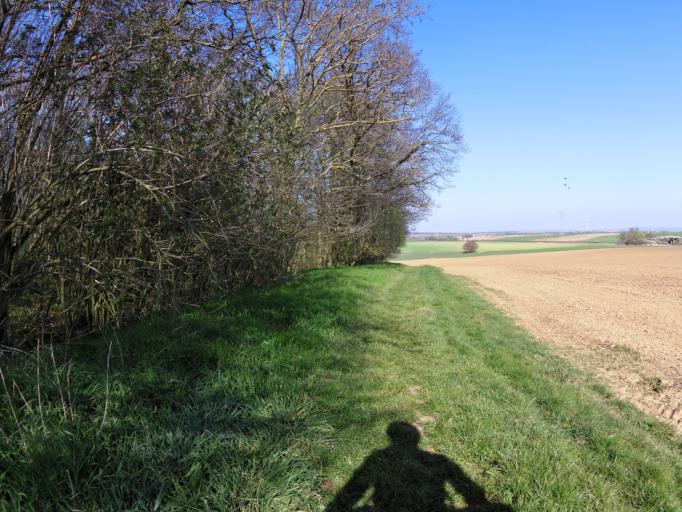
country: DE
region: Bavaria
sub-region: Regierungsbezirk Unterfranken
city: Kurnach
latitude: 49.8275
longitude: 10.0721
